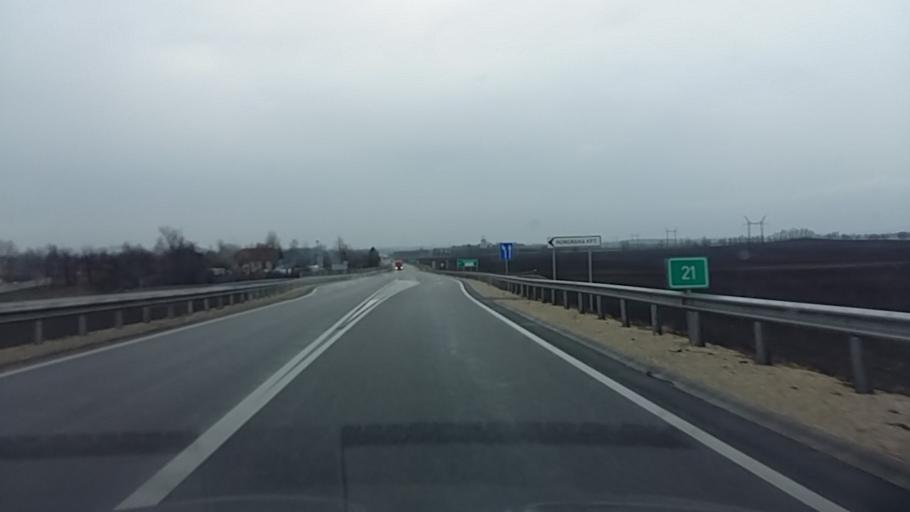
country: HU
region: Fejer
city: Sarosd
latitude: 47.0838
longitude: 18.7086
